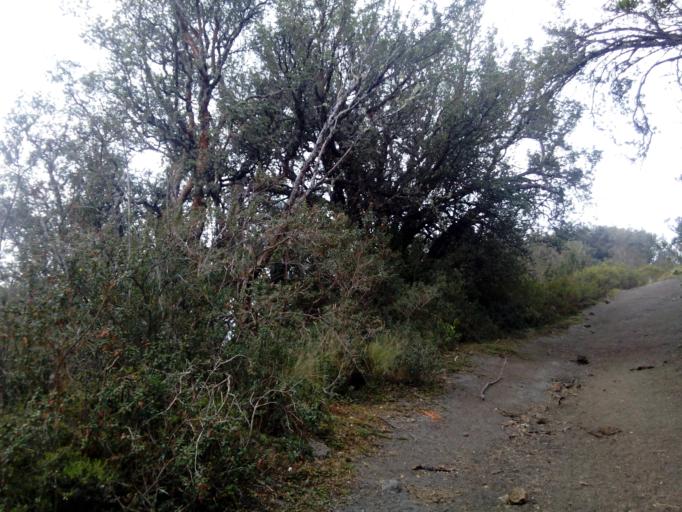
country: EC
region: Pichincha
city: Machachi
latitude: -0.5604
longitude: -78.5262
